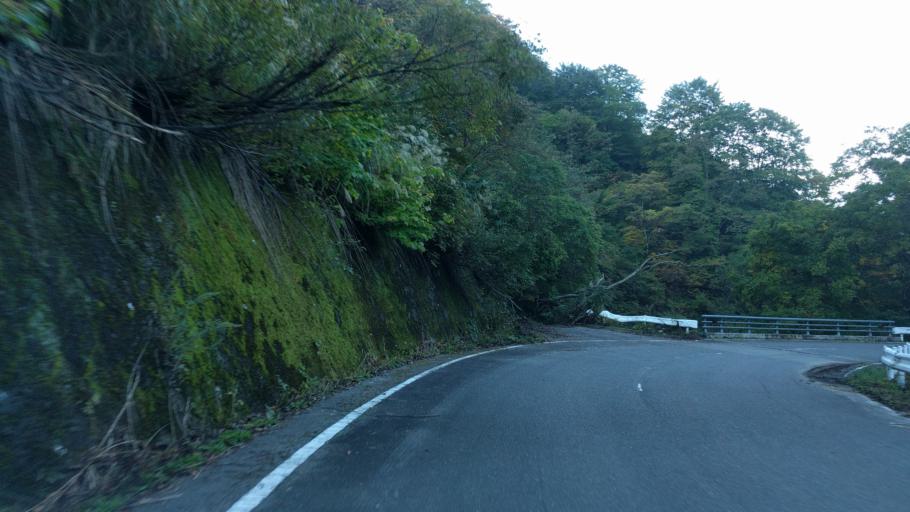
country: JP
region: Fukushima
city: Kitakata
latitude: 37.3936
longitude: 139.7547
